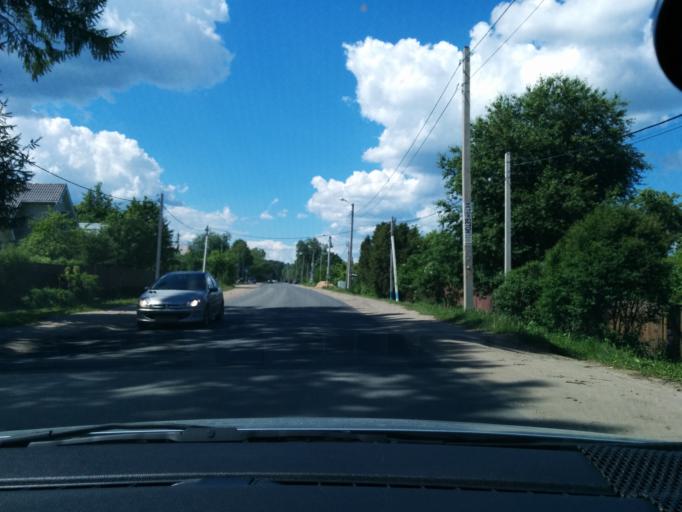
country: RU
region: Moskovskaya
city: Marfino
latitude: 56.0492
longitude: 37.5360
